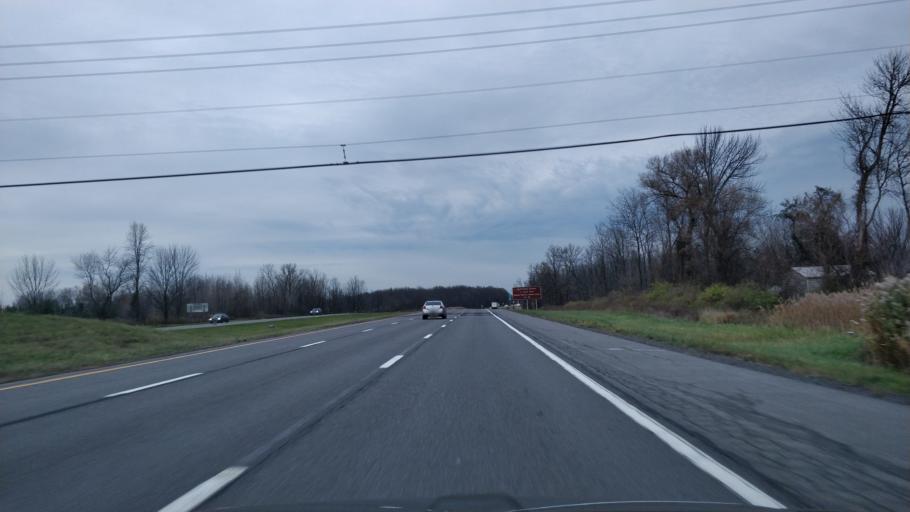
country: US
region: New York
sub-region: Onondaga County
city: Brewerton
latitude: 43.2168
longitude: -76.1294
